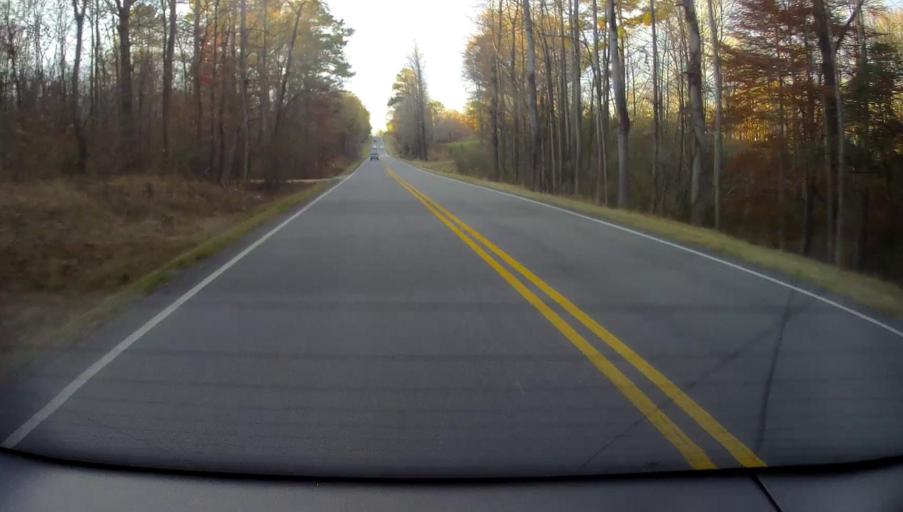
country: US
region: Alabama
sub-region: Blount County
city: Oneonta
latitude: 34.0855
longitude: -86.3465
